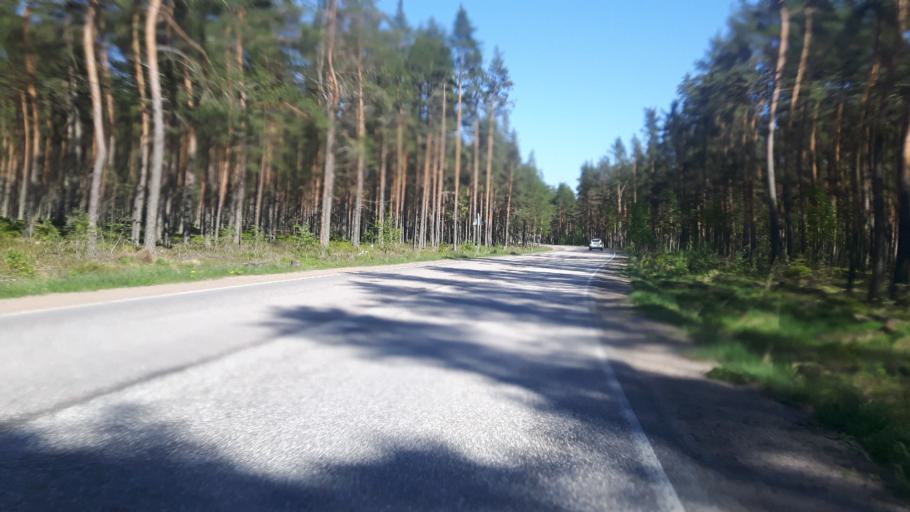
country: RU
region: Leningrad
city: Glebychevo
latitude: 60.2768
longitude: 28.9117
